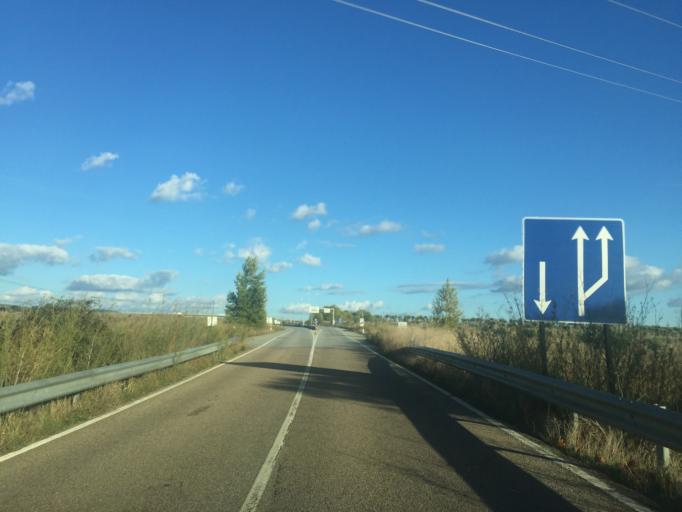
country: PT
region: Portalegre
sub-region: Alter do Chao
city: Alter do Chao
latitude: 39.1969
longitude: -7.7036
